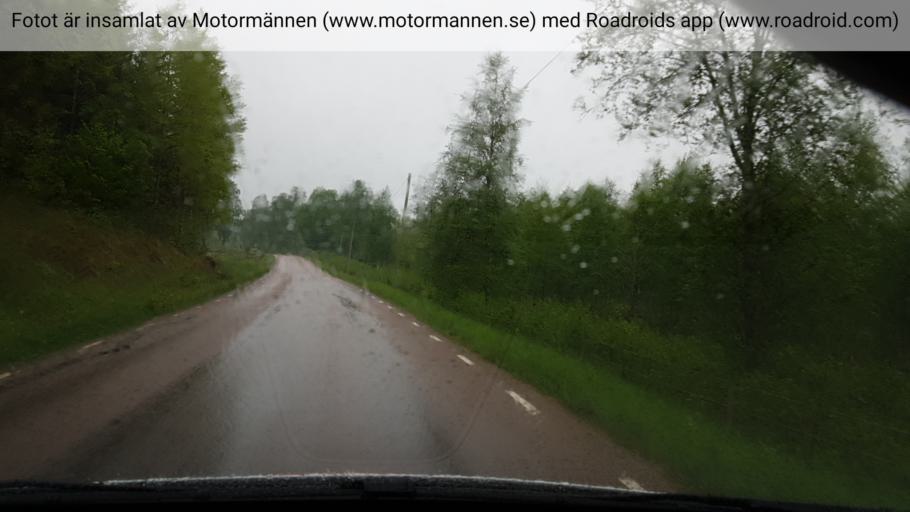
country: SE
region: Vaestra Goetaland
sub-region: Ulricehamns Kommun
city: Ulricehamn
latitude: 57.8296
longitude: 13.4597
